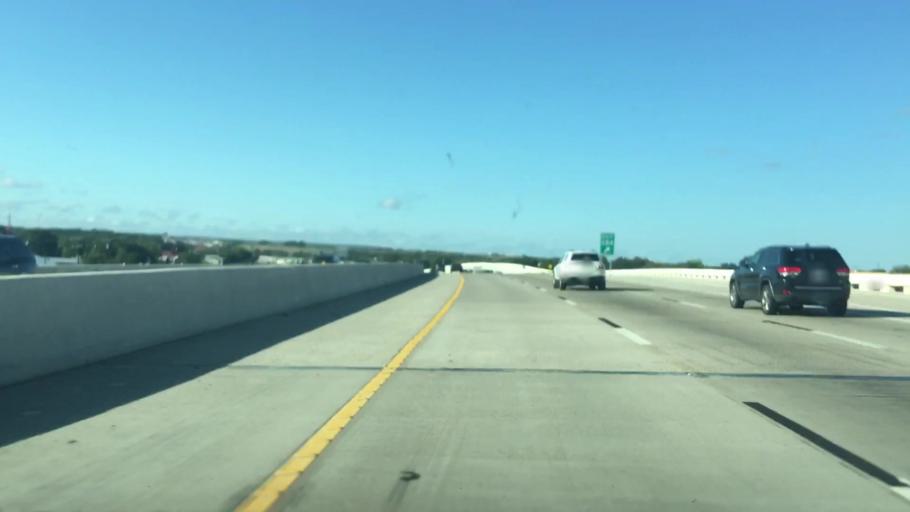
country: US
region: Texas
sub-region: Bell County
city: Salado
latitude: 30.9561
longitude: -97.5355
